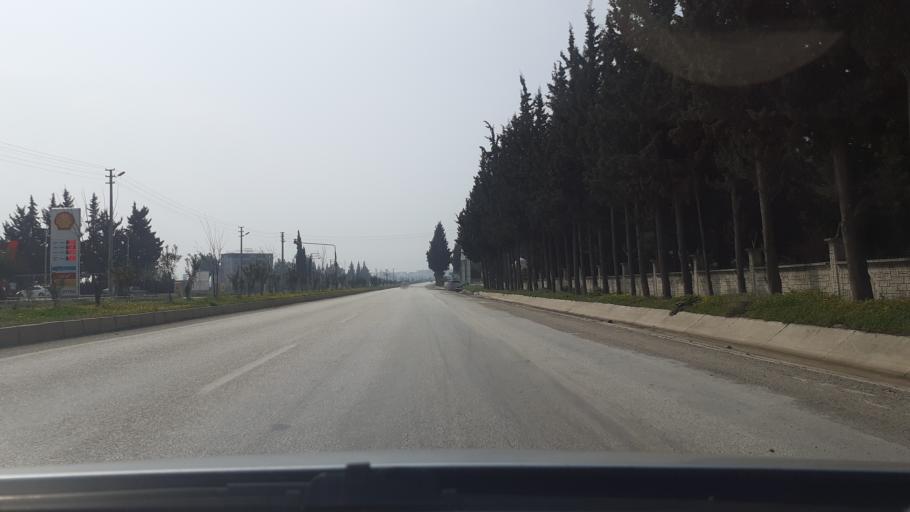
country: TR
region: Hatay
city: Kirikhan
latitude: 36.5212
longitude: 36.3766
